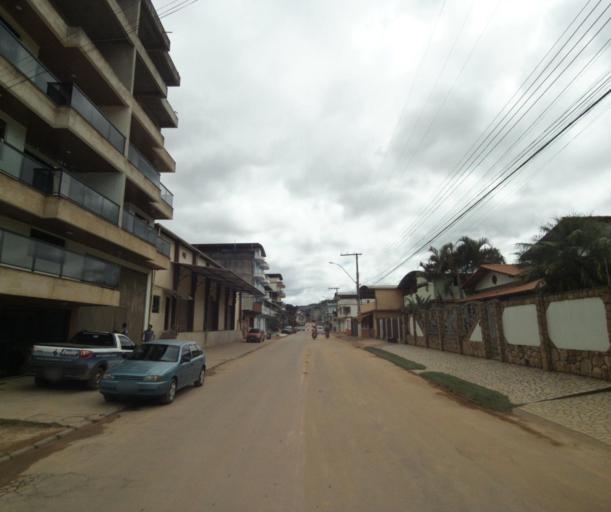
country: BR
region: Espirito Santo
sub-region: Irupi
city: Irupi
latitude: -20.3492
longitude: -41.6371
